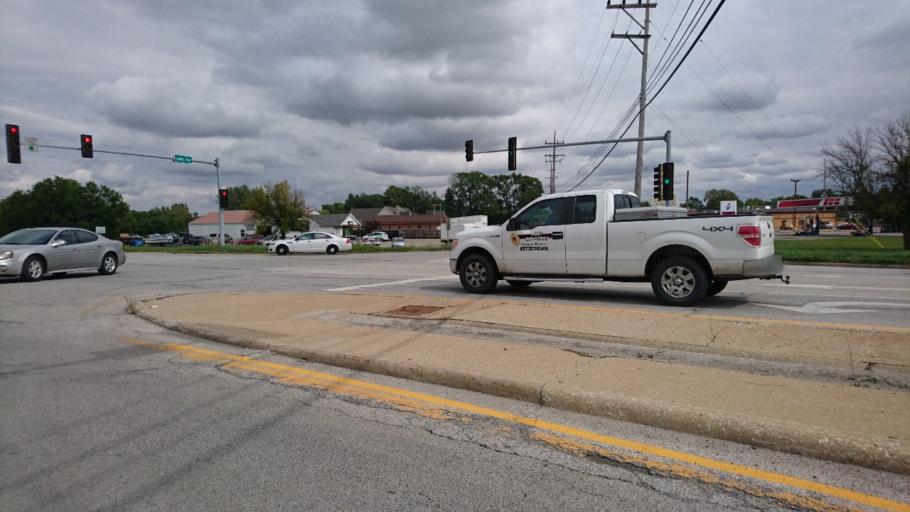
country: US
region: Illinois
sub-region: Livingston County
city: Pontiac
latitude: 40.8864
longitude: -88.6423
